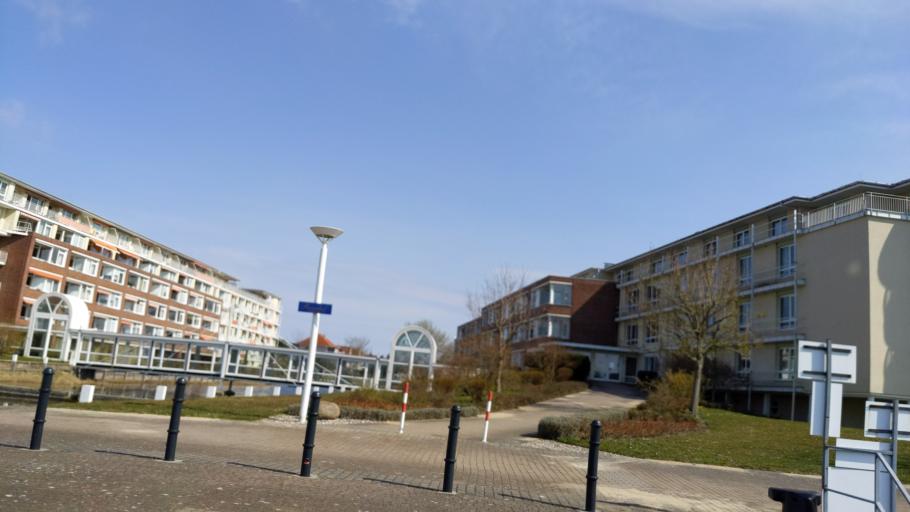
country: DE
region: Schleswig-Holstein
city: Travemuende
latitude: 53.9533
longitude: 10.8698
